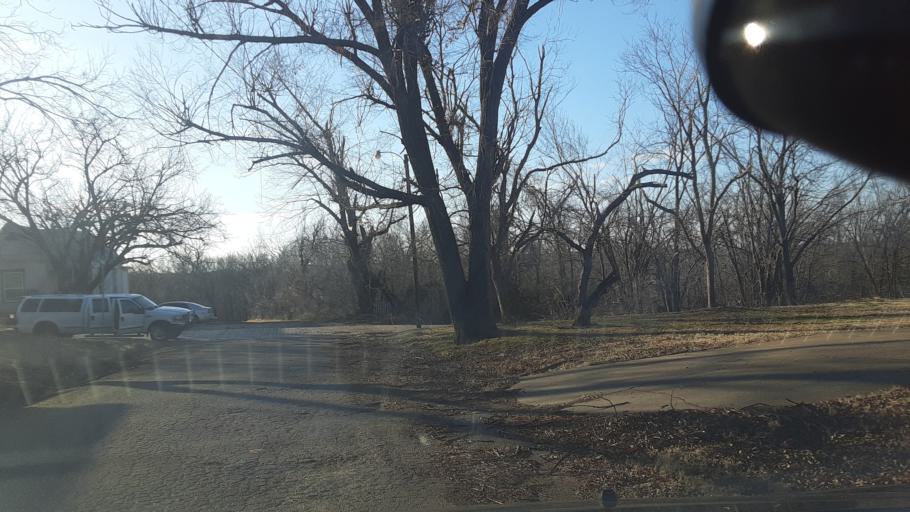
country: US
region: Oklahoma
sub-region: Logan County
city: Guthrie
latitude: 35.8822
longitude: -97.4262
